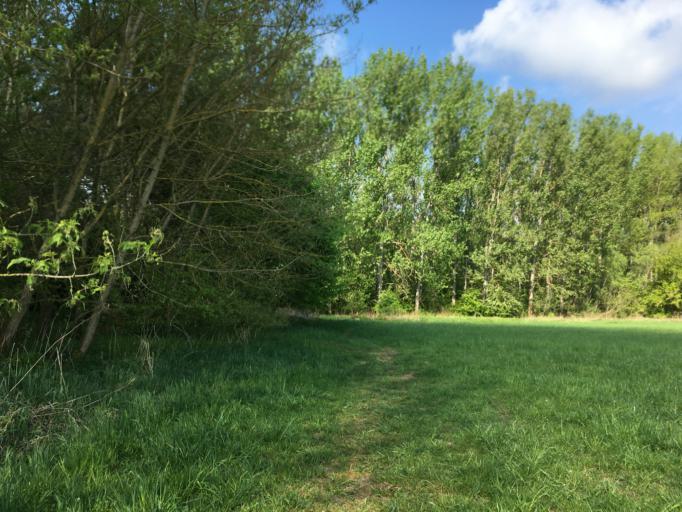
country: DE
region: Berlin
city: Blankenfelde
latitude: 52.6125
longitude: 13.3998
